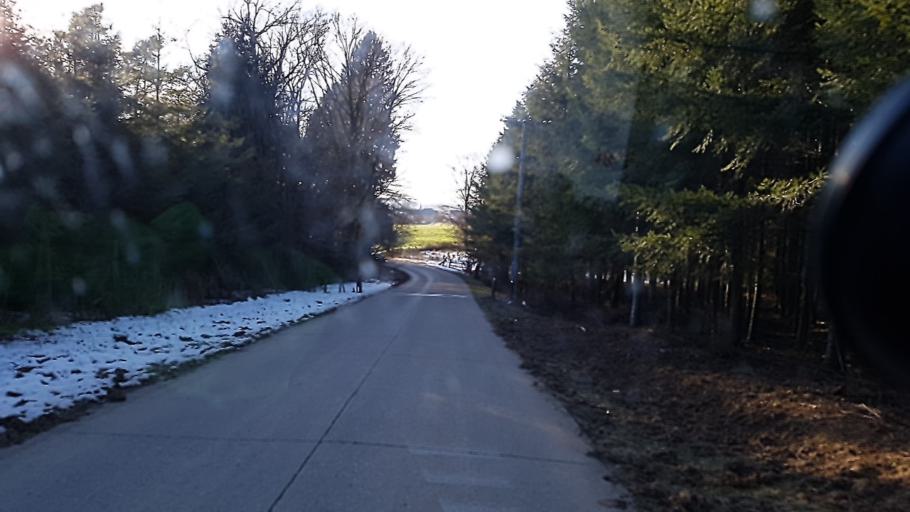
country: BE
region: Wallonia
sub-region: Province du Luxembourg
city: Daverdisse
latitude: 50.0067
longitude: 5.1762
